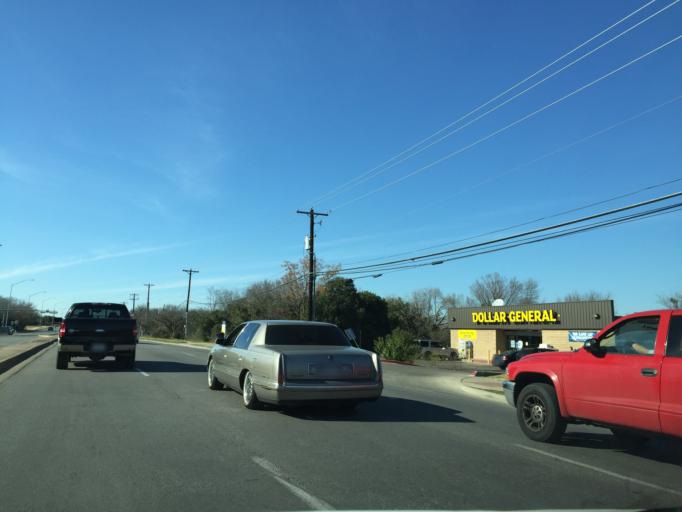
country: US
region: Texas
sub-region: Travis County
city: Austin
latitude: 30.2263
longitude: -97.7062
